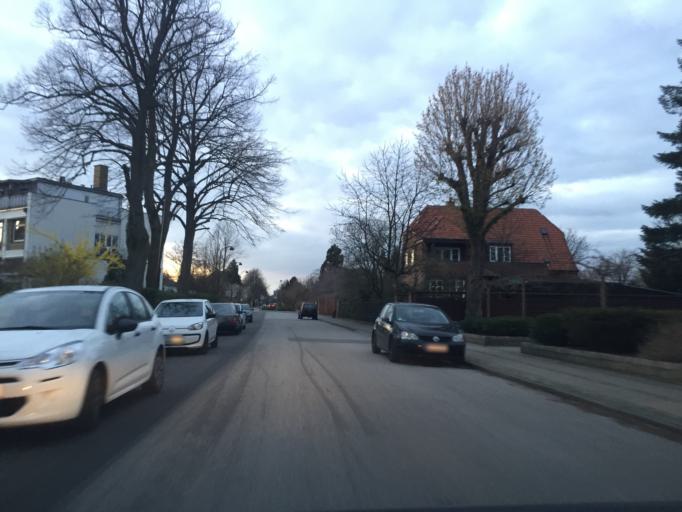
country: DK
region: Capital Region
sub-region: Gentofte Kommune
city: Charlottenlund
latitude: 55.7347
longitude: 12.5646
